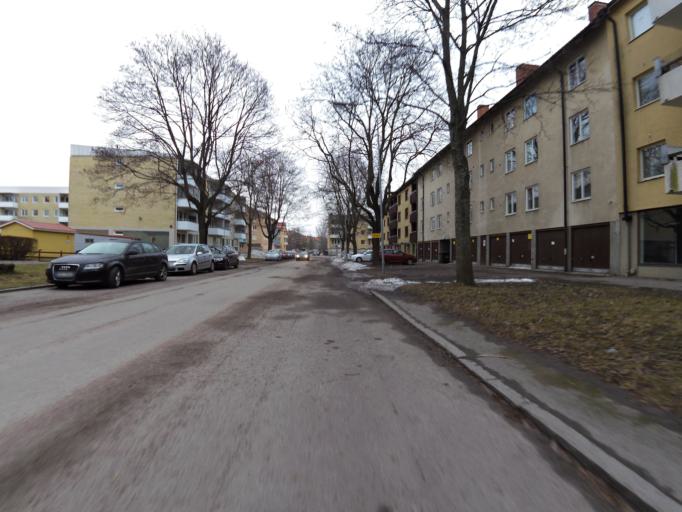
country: SE
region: Gaevleborg
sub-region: Gavle Kommun
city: Gavle
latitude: 60.6666
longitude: 17.1571
